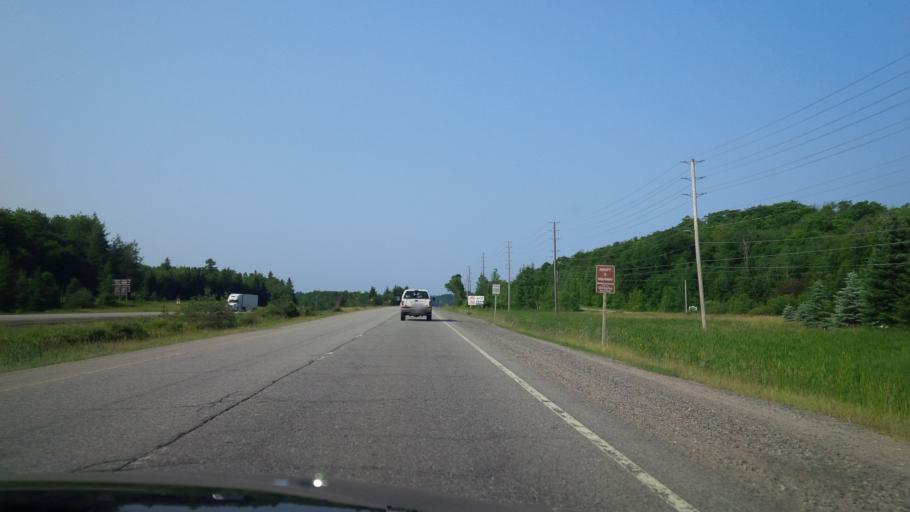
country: CA
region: Ontario
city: Huntsville
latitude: 45.2756
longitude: -79.2814
